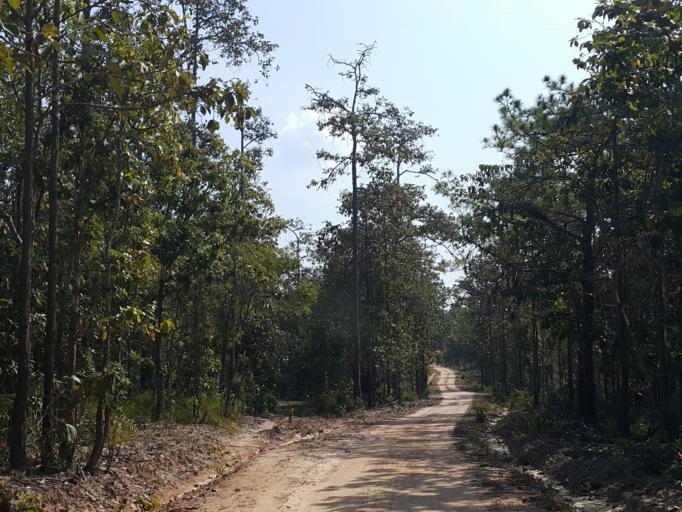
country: TH
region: Chiang Mai
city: Hot
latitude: 18.1322
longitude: 98.4346
